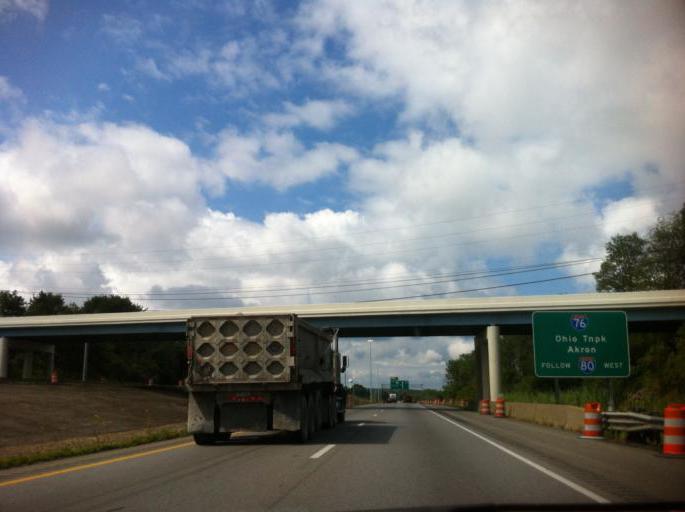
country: US
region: Ohio
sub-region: Trumbull County
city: Mineral Ridge
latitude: 41.1339
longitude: -80.7375
